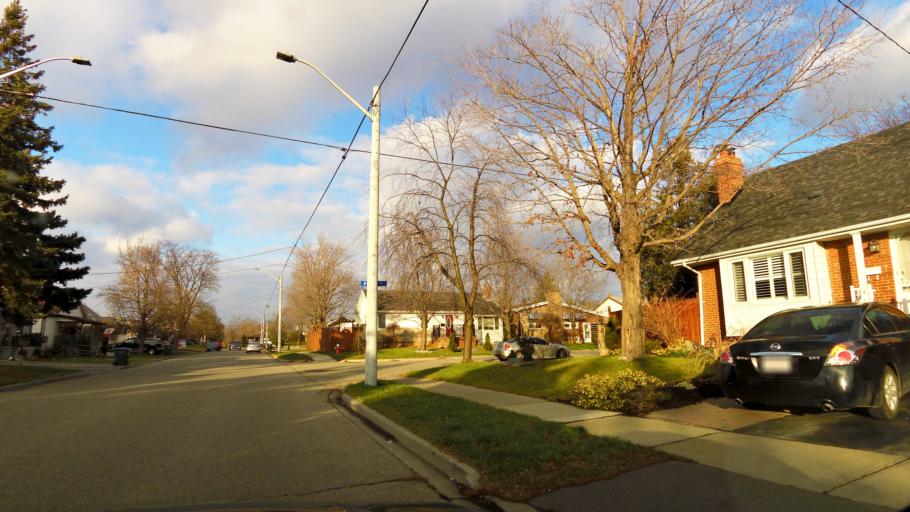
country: CA
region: Ontario
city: Etobicoke
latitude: 43.7023
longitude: -79.6476
